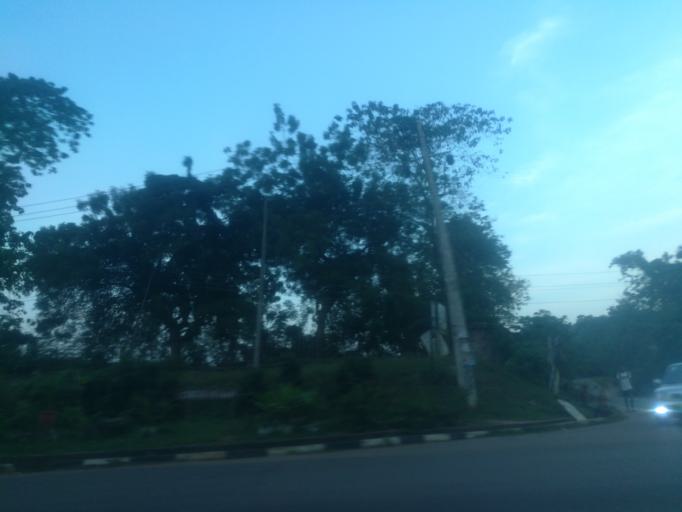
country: NG
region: Ogun
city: Abeokuta
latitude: 7.1373
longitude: 3.3437
